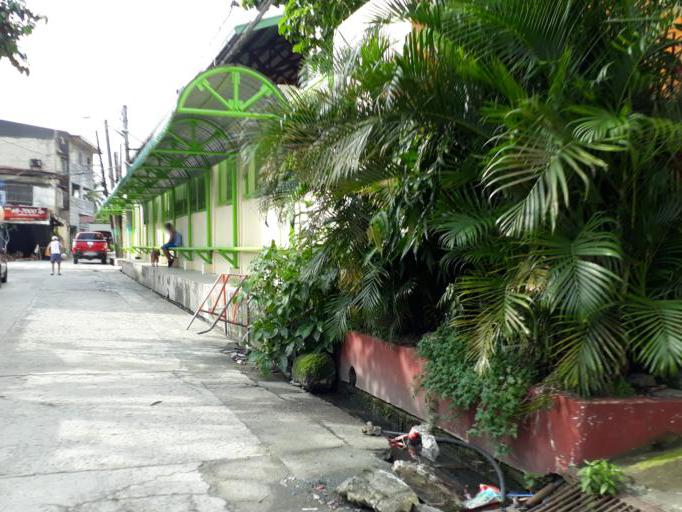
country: PH
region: Calabarzon
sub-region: Province of Rizal
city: Valenzuela
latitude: 14.6760
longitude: 120.9908
